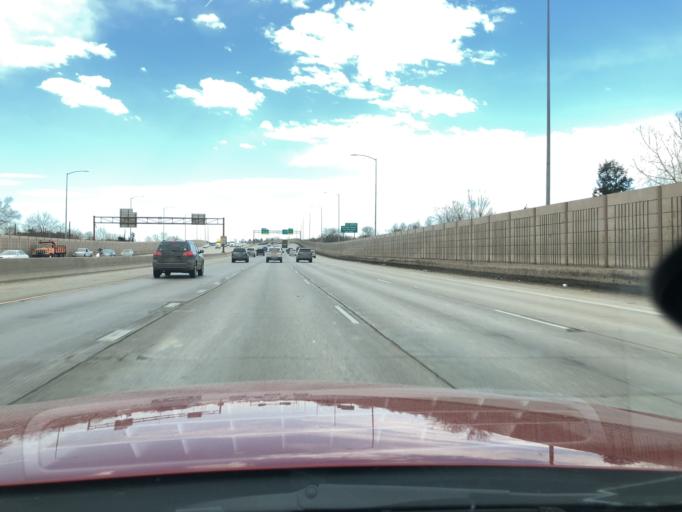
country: US
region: Colorado
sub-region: Jefferson County
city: Arvada
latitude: 39.7836
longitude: -105.0969
